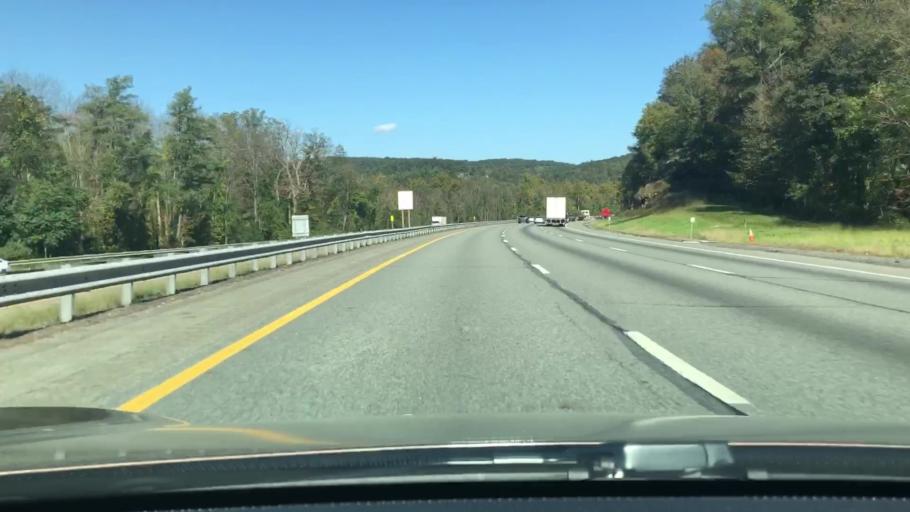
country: US
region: New York
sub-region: Rockland County
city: Sloatsburg
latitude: 41.2210
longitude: -74.1842
